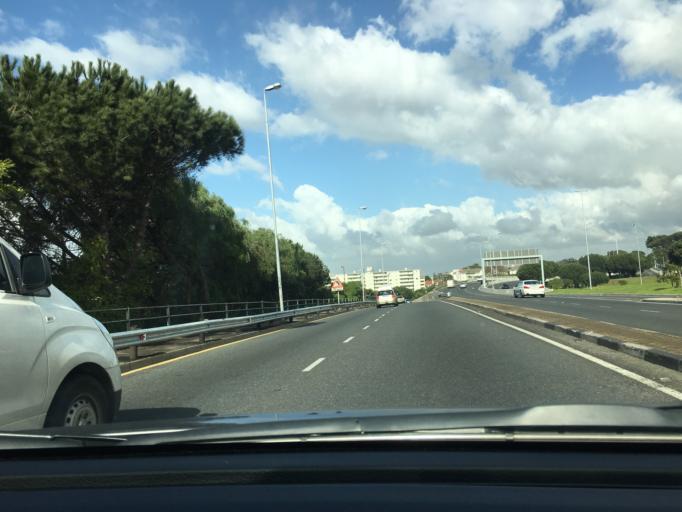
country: ZA
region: Western Cape
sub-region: City of Cape Town
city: Rosebank
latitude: -33.9444
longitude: 18.4659
